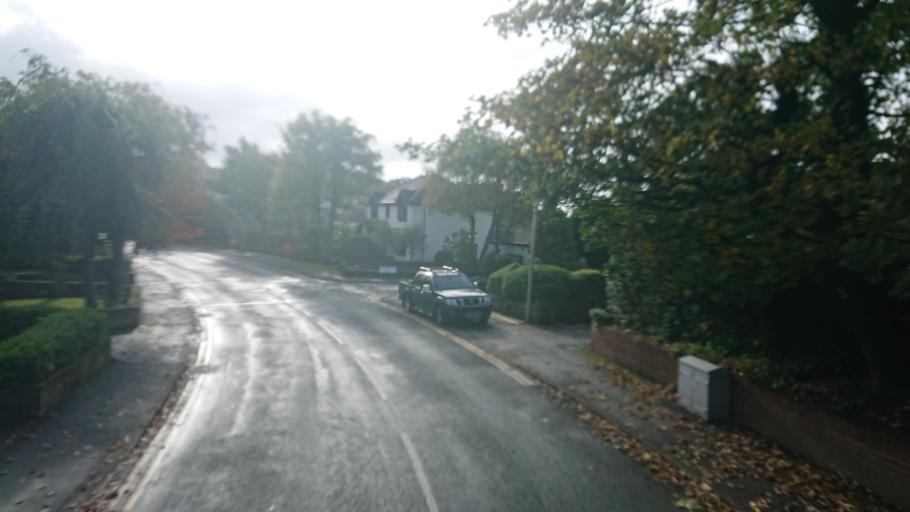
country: GB
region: England
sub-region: Lancashire
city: Bolton le Sands
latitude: 54.0859
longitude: -2.8091
